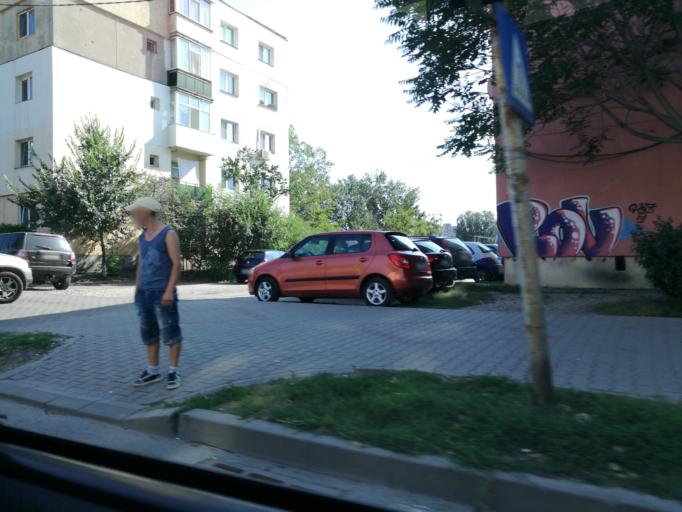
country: RO
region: Iasi
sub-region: Municipiul Iasi
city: Iasi
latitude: 47.1696
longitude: 27.5643
